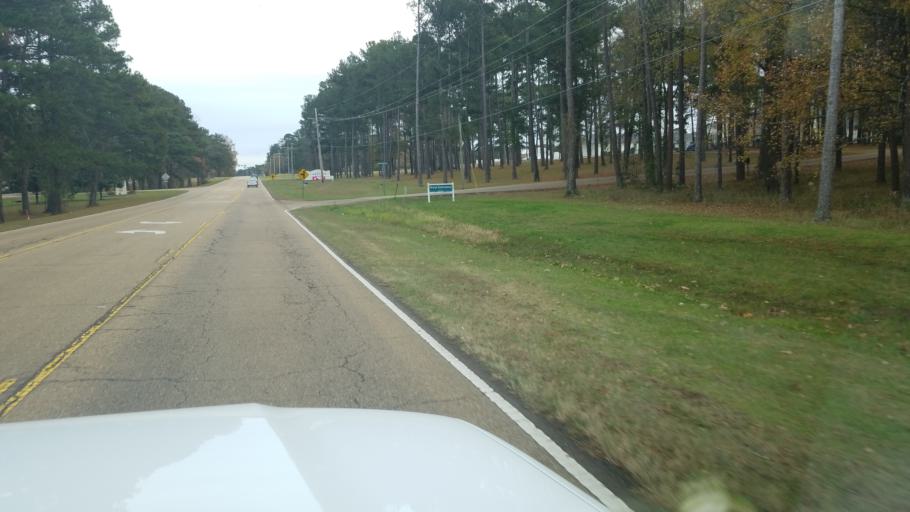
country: US
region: Mississippi
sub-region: Rankin County
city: Brandon
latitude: 32.3768
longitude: -90.0274
